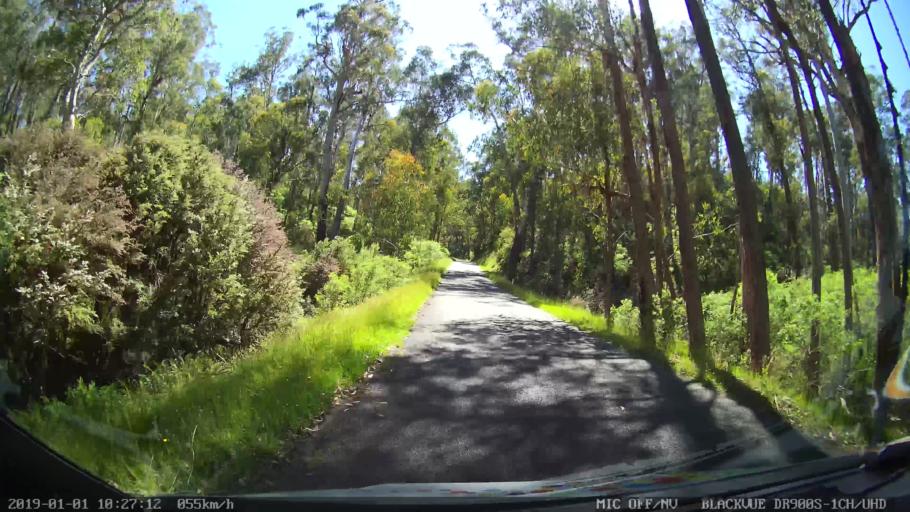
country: AU
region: New South Wales
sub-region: Snowy River
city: Jindabyne
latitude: -36.0670
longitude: 148.2349
